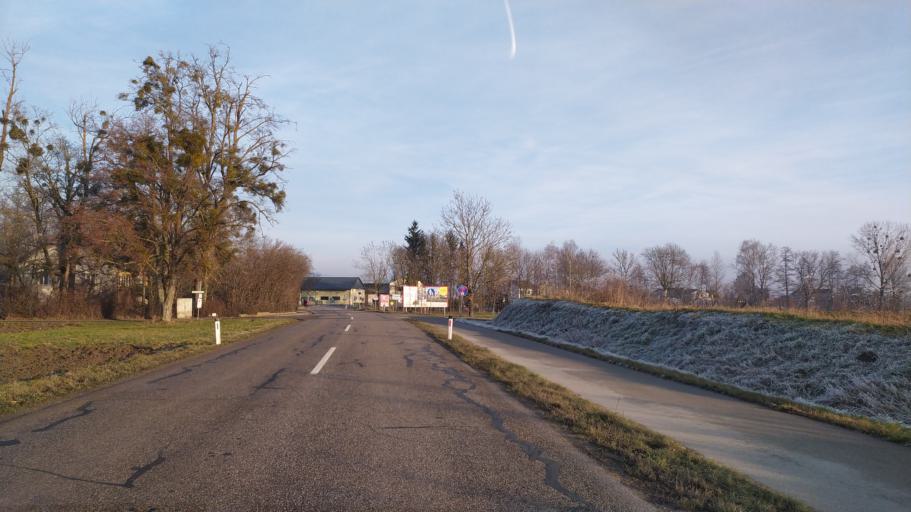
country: AT
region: Upper Austria
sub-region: Politischer Bezirk Urfahr-Umgebung
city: Feldkirchen an der Donau
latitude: 48.3476
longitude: 14.0689
